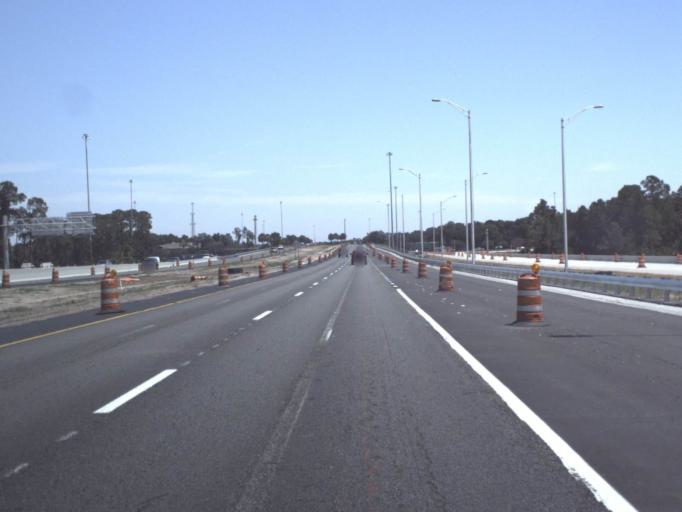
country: US
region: Florida
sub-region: Duval County
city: Jacksonville
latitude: 30.4066
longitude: -81.5646
